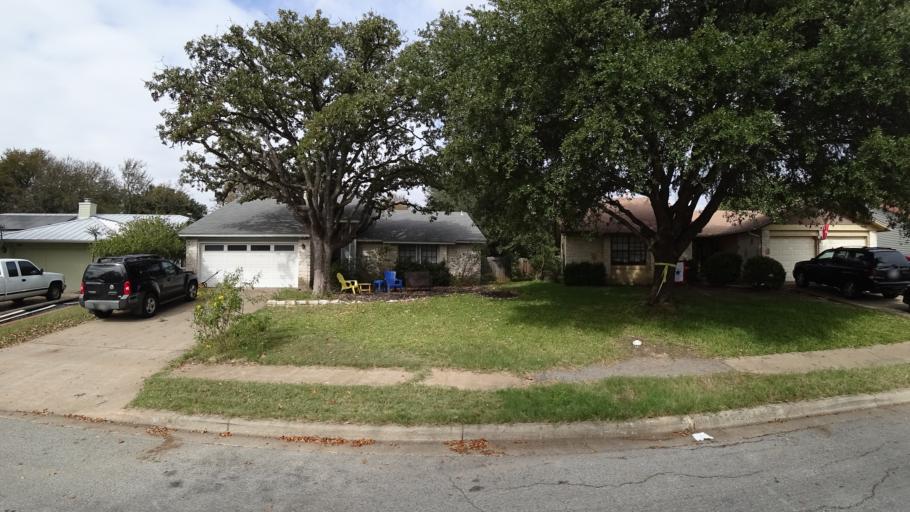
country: US
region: Texas
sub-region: Travis County
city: Wells Branch
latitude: 30.4266
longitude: -97.7087
